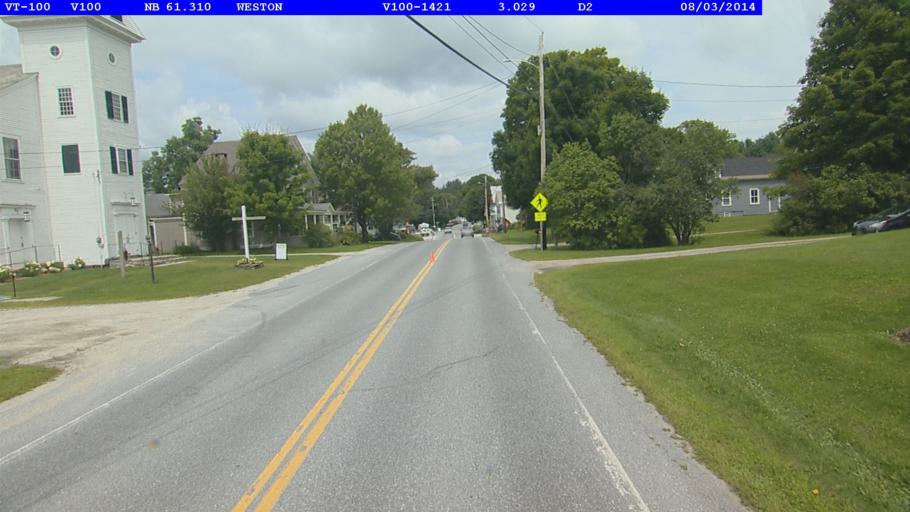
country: US
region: Vermont
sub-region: Windsor County
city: Chester
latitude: 43.2894
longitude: -72.7931
